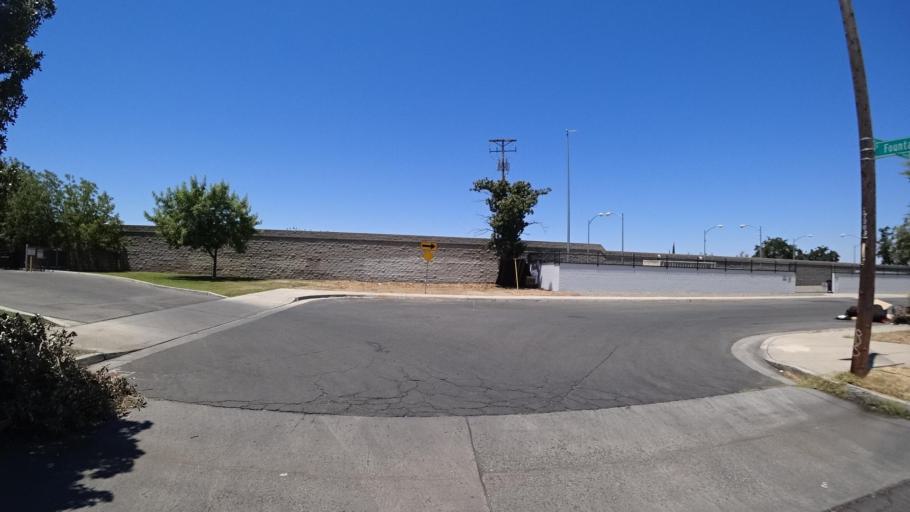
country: US
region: California
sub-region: Fresno County
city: Fresno
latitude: 36.7814
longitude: -119.7480
